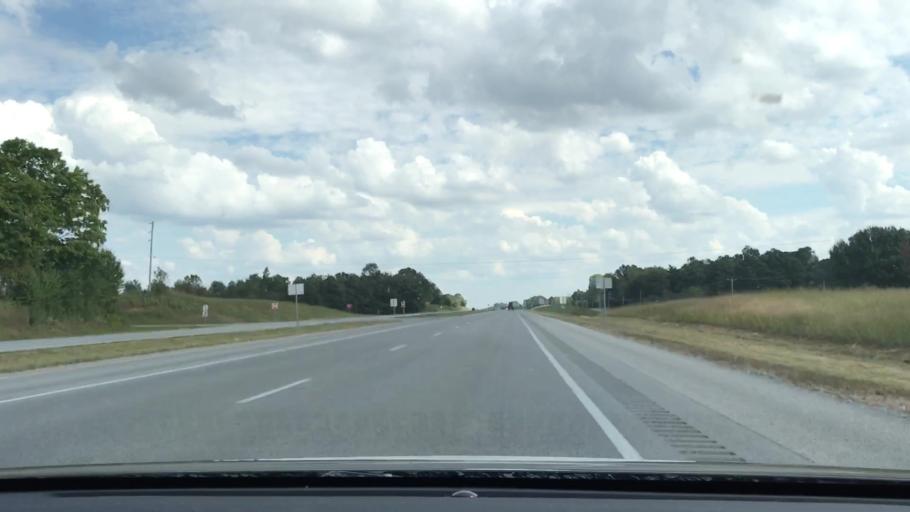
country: US
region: Kentucky
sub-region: Trigg County
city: Cadiz
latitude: 36.8684
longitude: -87.7754
